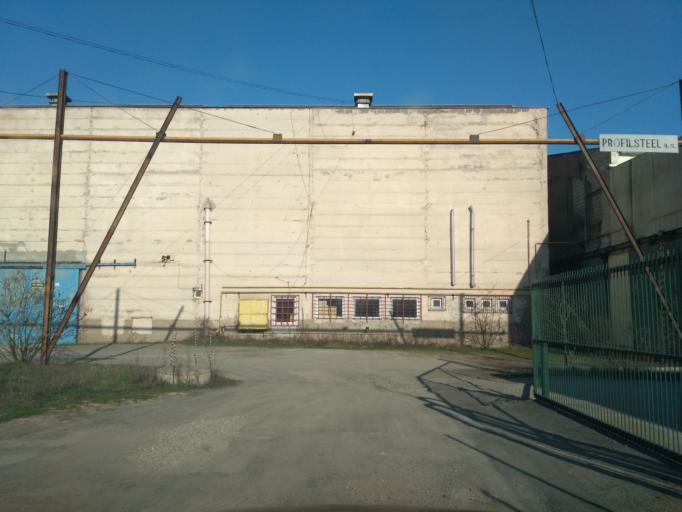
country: SK
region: Kosicky
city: Kosice
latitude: 48.6733
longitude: 21.2926
